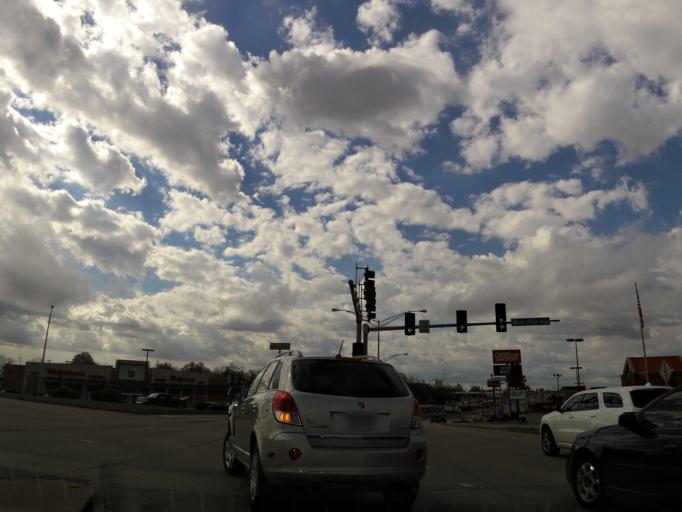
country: US
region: Missouri
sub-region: Butler County
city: Poplar Bluff
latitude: 36.7587
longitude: -90.4077
